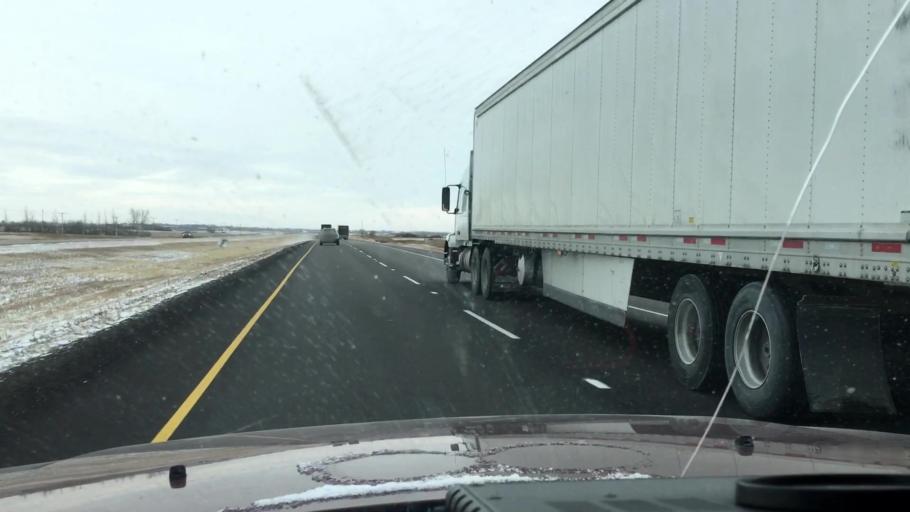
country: CA
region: Saskatchewan
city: Saskatoon
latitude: 51.7896
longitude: -106.4828
